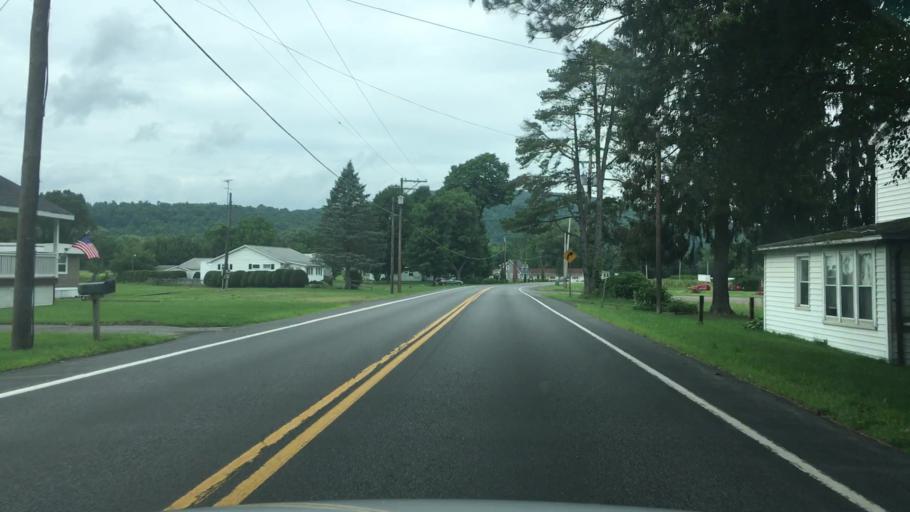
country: US
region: New York
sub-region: Otsego County
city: Otego
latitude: 42.4198
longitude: -75.1430
